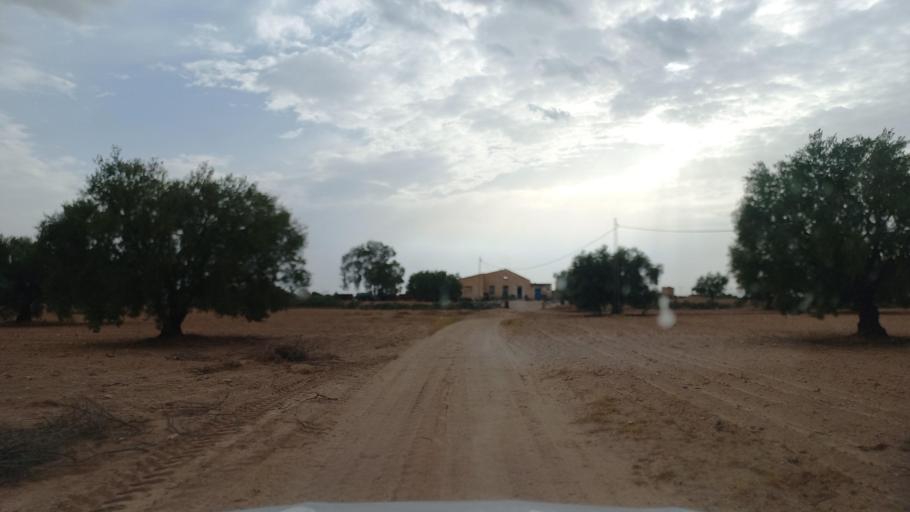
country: TN
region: Al Qasrayn
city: Sbiba
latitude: 35.2958
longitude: 9.0772
